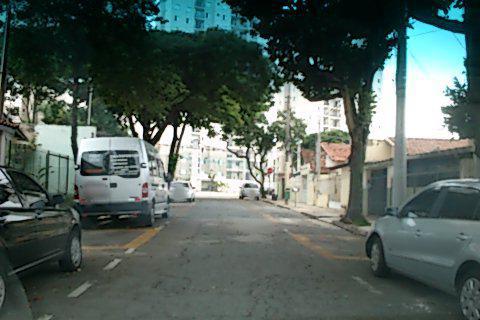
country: BR
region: Sao Paulo
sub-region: Sao Jose Dos Campos
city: Sao Jose dos Campos
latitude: -23.1965
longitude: -45.8782
